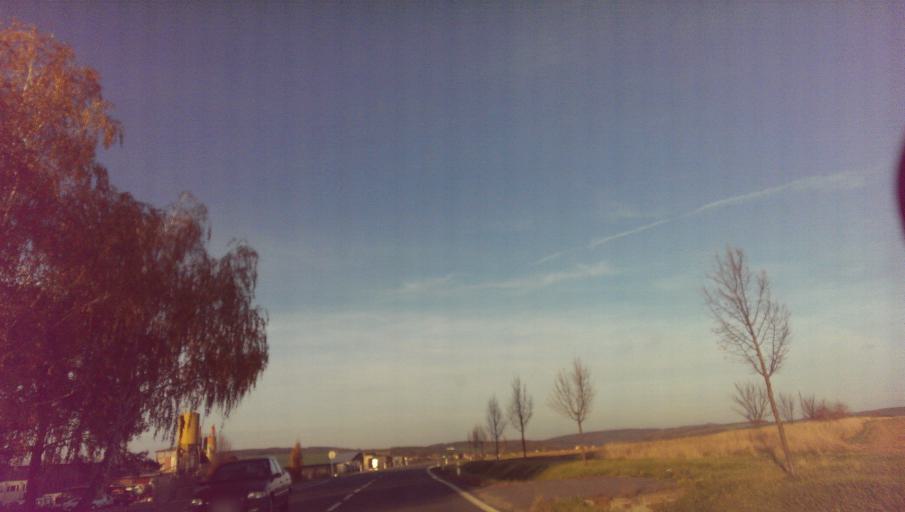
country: CZ
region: Zlin
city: Bilovice
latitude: 49.1062
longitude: 17.5585
